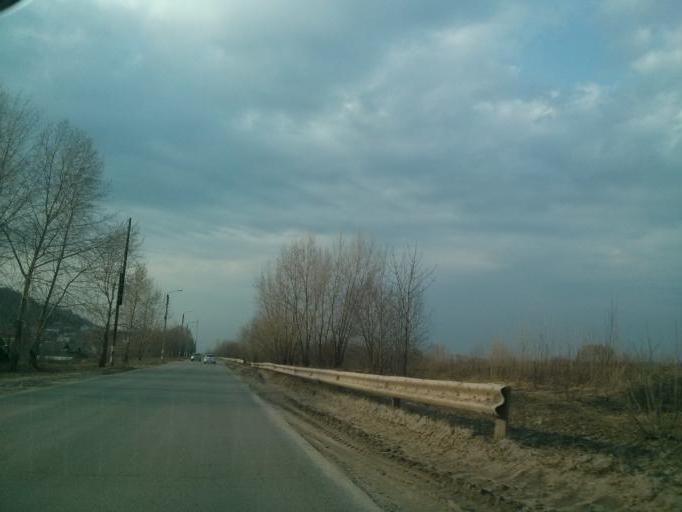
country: RU
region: Nizjnij Novgorod
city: Afonino
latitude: 56.3010
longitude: 44.1024
